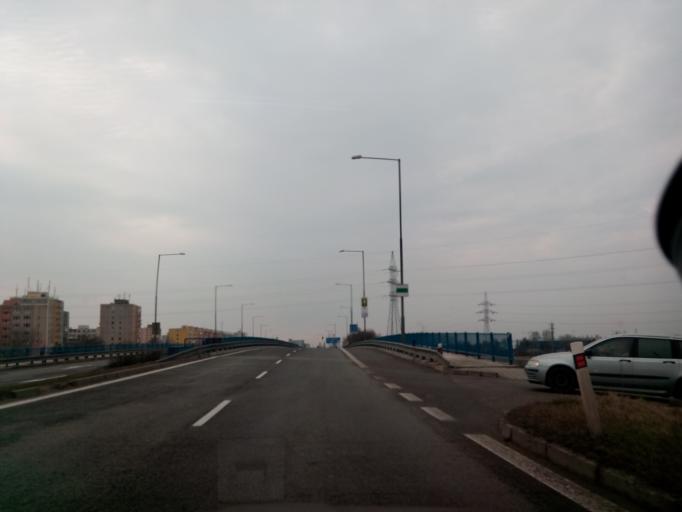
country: SK
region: Kosicky
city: Kosice
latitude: 48.7004
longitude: 21.2803
